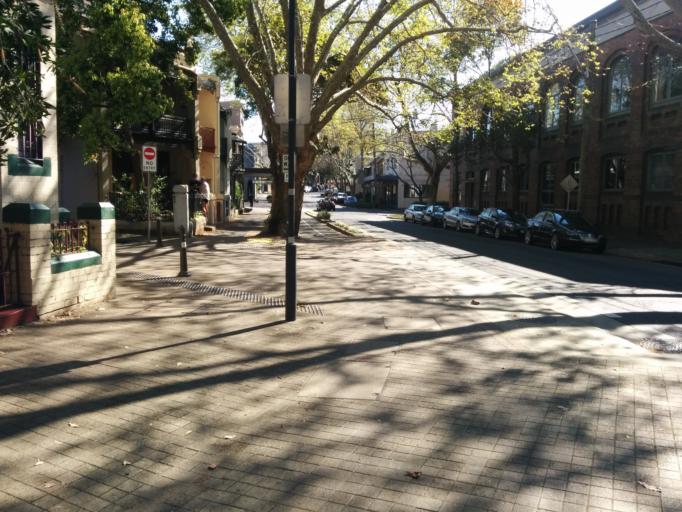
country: AU
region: New South Wales
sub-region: City of Sydney
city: Darlinghurst
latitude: -33.8883
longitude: 151.2153
